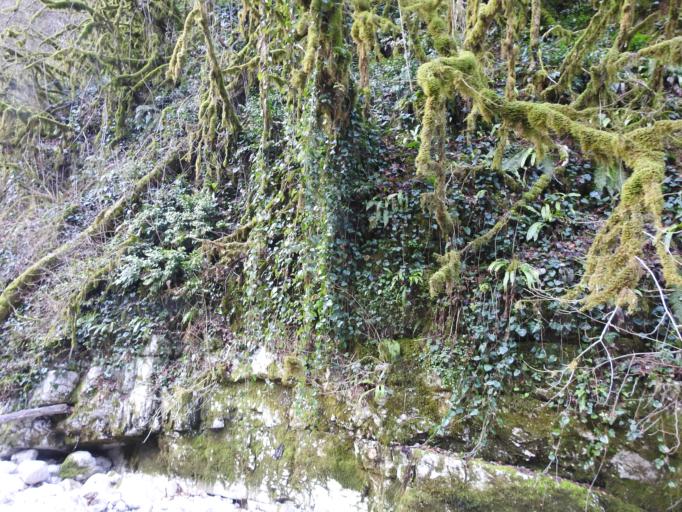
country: GE
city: Gantiadi
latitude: 43.4140
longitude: 40.2162
